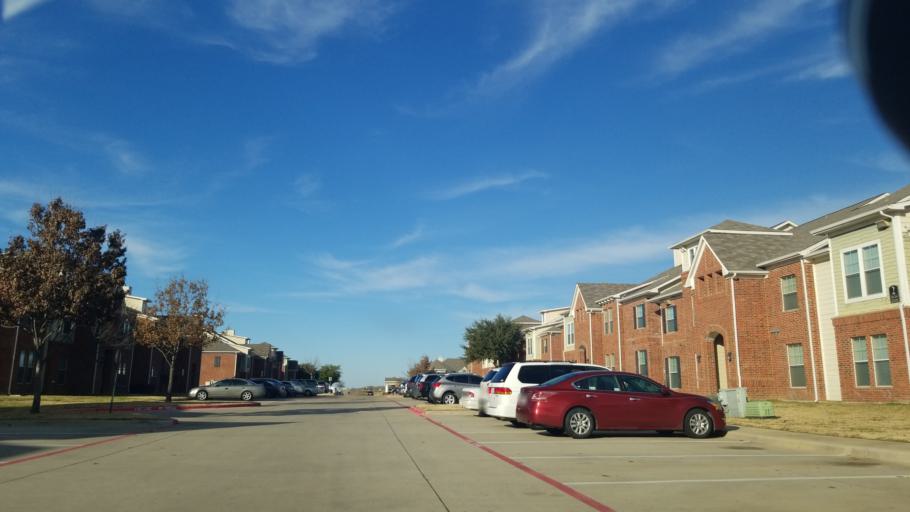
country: US
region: Texas
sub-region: Denton County
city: Corinth
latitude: 33.1408
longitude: -97.0565
